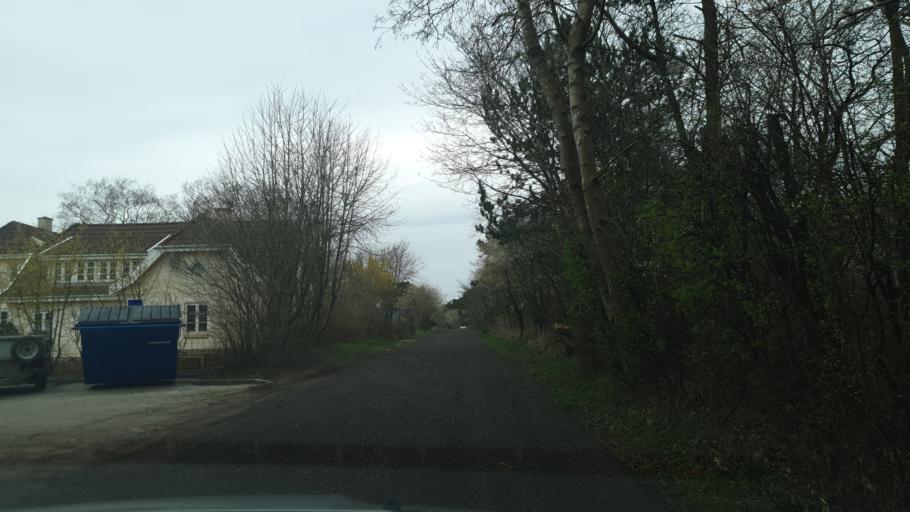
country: DK
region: Zealand
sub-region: Odsherred Kommune
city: Asnaes
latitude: 55.8331
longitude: 11.4198
